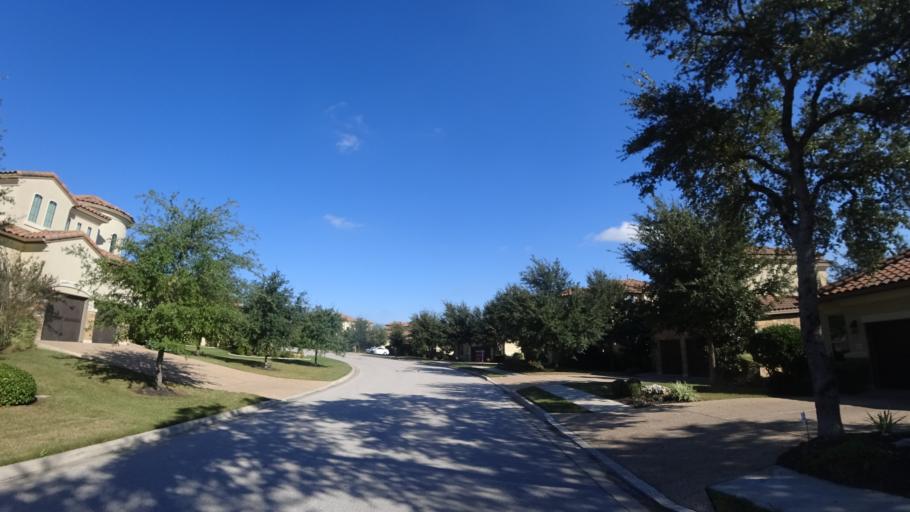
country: US
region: Texas
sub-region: Travis County
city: Bee Cave
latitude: 30.3478
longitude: -97.8929
